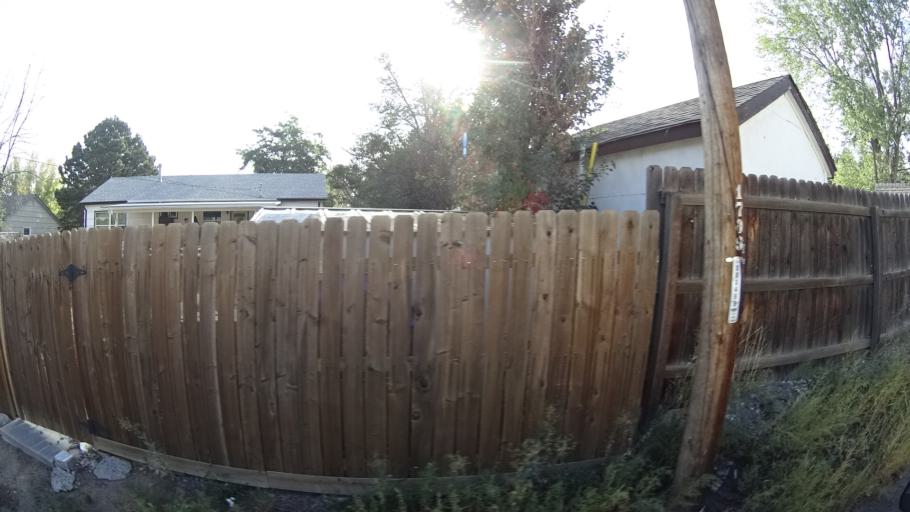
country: US
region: Colorado
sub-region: El Paso County
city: Colorado Springs
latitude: 38.8570
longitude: -104.7681
